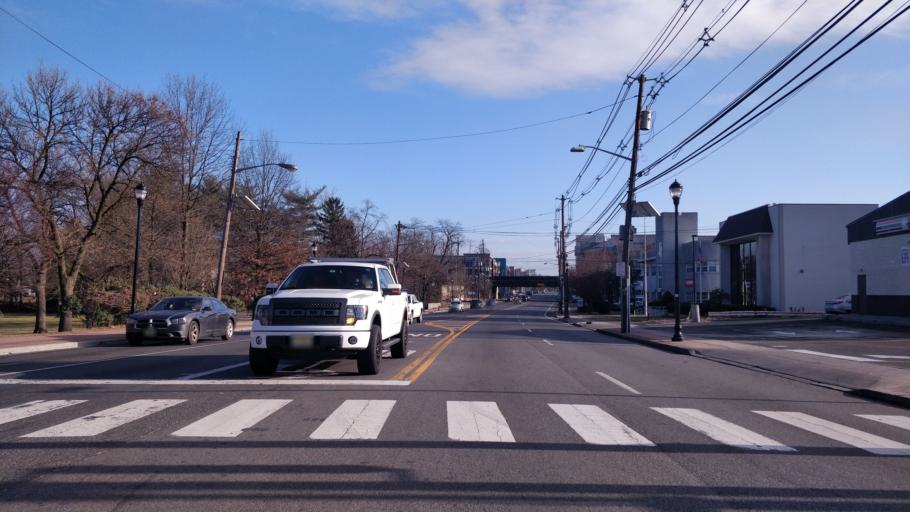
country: US
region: New Jersey
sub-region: Union County
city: Hillside
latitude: 40.6858
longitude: -74.2397
